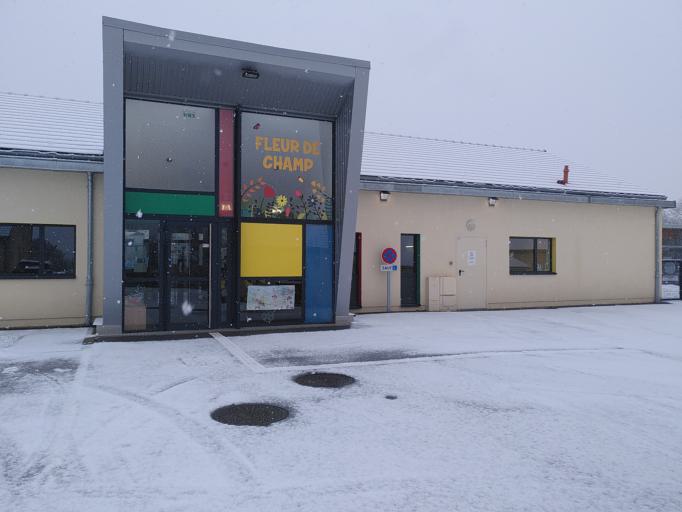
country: FR
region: Lorraine
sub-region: Departement de Meurthe-et-Moselle
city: Champenoux
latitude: 48.7432
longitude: 6.3471
